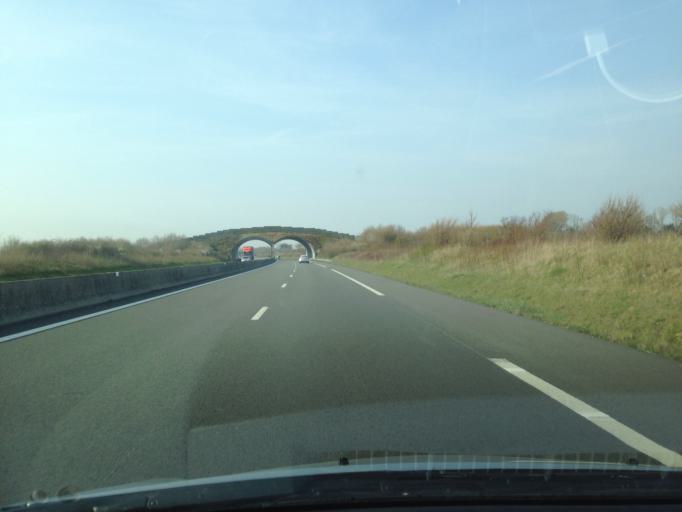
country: FR
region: Picardie
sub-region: Departement de la Somme
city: Nouvion
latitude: 50.2567
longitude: 1.7484
